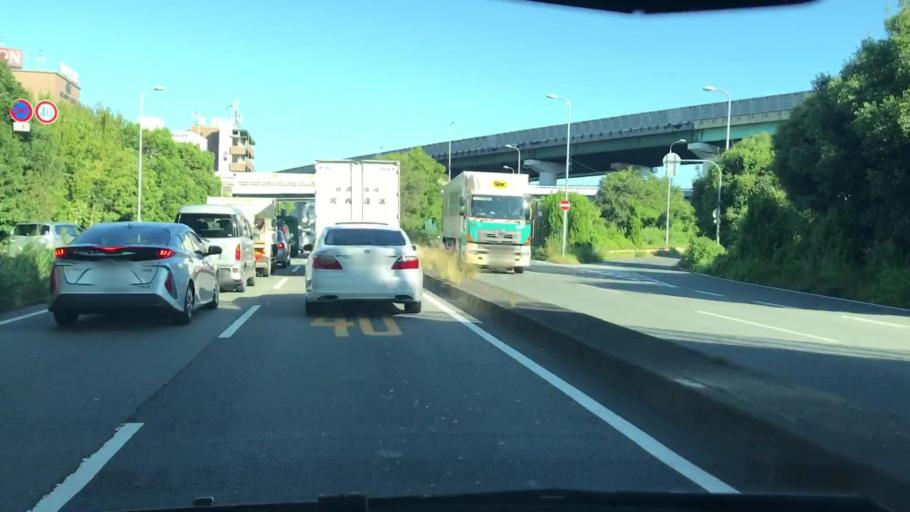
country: JP
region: Osaka
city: Ikeda
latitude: 34.7998
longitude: 135.4392
